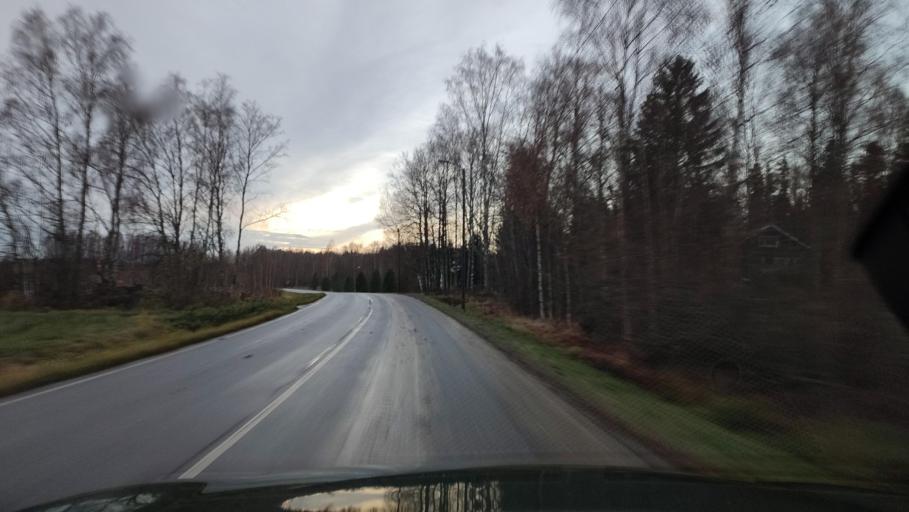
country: FI
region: Ostrobothnia
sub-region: Vaasa
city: Ristinummi
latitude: 63.0479
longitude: 21.7400
